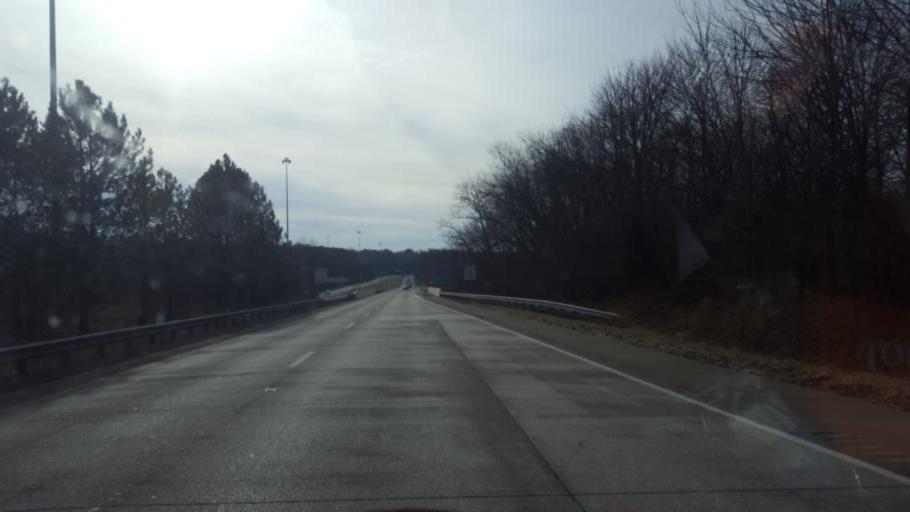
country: US
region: Ohio
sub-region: Wayne County
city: Wooster
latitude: 40.7968
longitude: -81.9163
